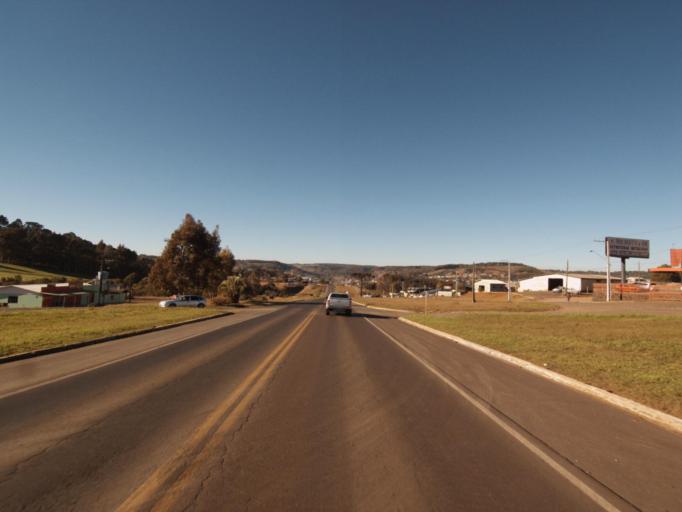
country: BR
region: Santa Catarina
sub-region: Concordia
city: Concordia
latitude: -26.8614
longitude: -52.0265
